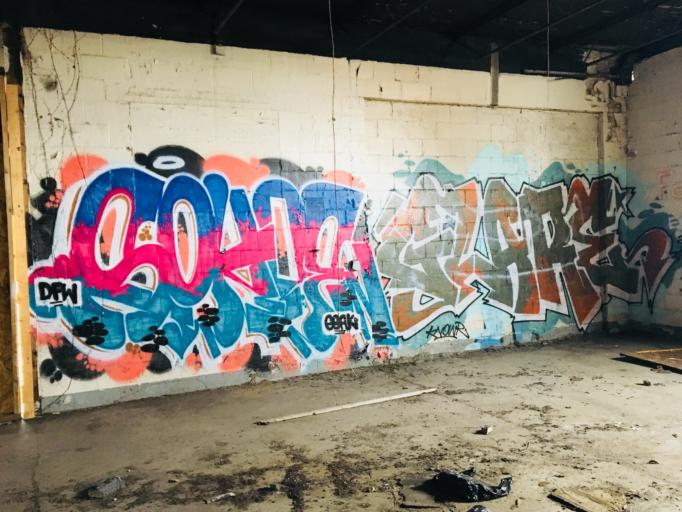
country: US
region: Michigan
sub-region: Macomb County
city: Eastpointe
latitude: 42.4162
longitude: -82.9895
